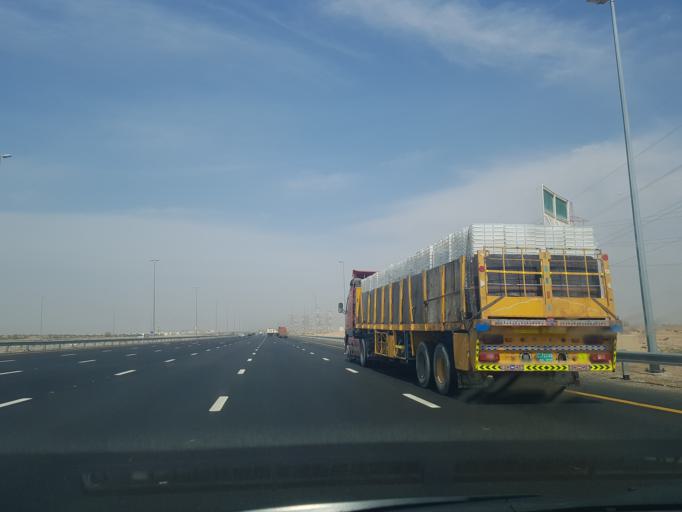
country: AE
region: Ash Shariqah
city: Sharjah
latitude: 25.2756
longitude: 55.5837
